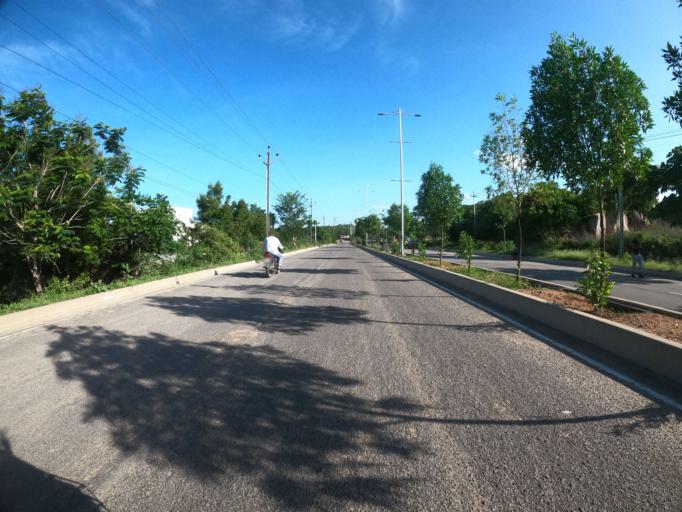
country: IN
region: Telangana
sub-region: Hyderabad
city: Hyderabad
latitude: 17.3526
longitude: 78.3698
